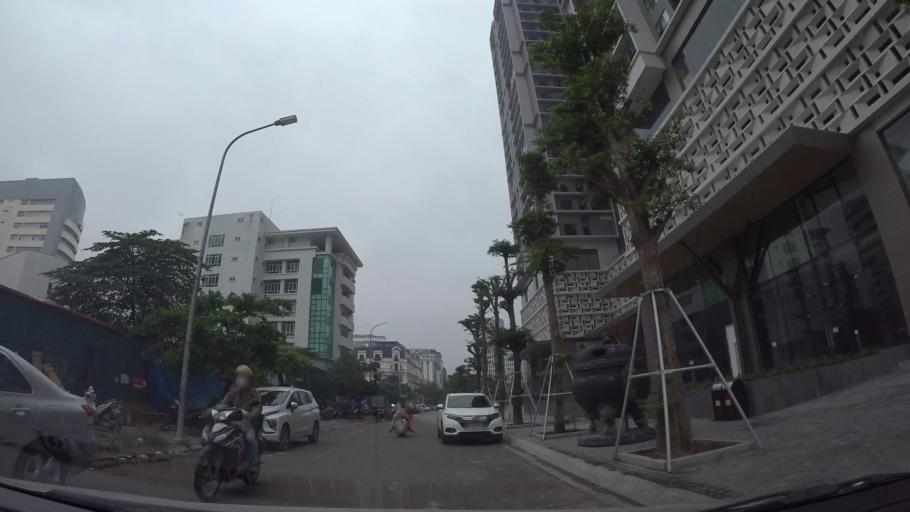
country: VN
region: Ha Noi
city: Cau Giay
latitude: 21.0268
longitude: 105.7857
